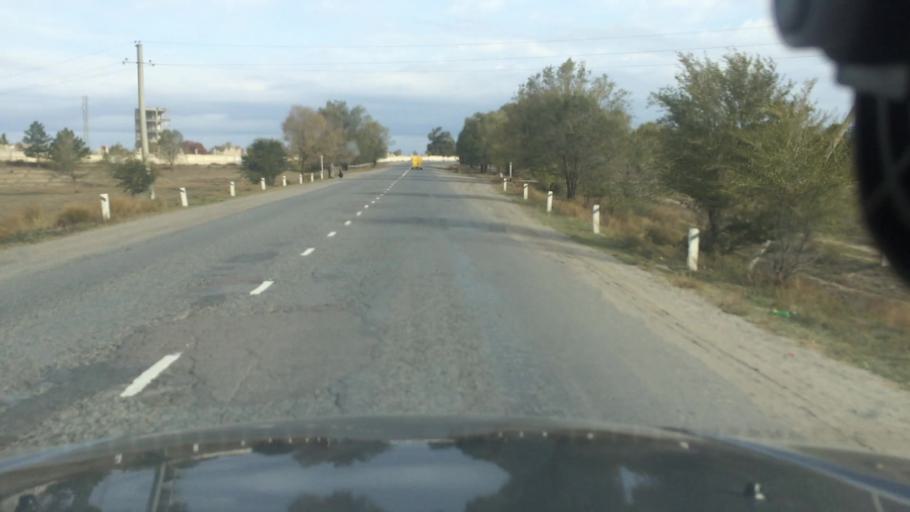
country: KG
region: Ysyk-Koel
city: Karakol
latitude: 42.5347
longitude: 78.3819
